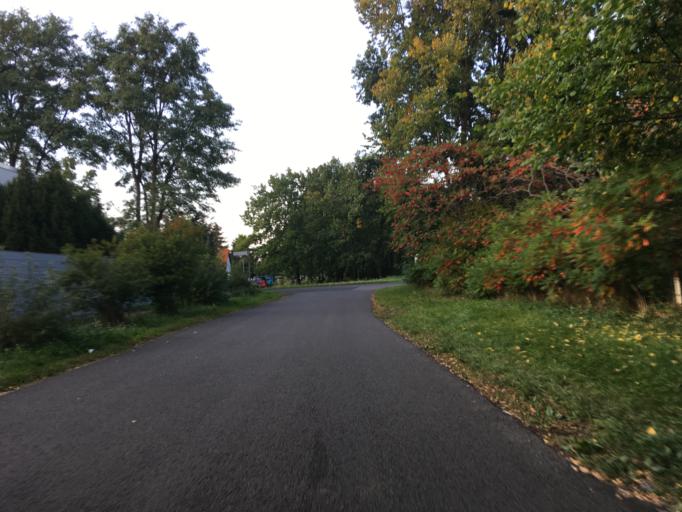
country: DE
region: Berlin
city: Biesdorf
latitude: 52.4948
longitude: 13.5586
